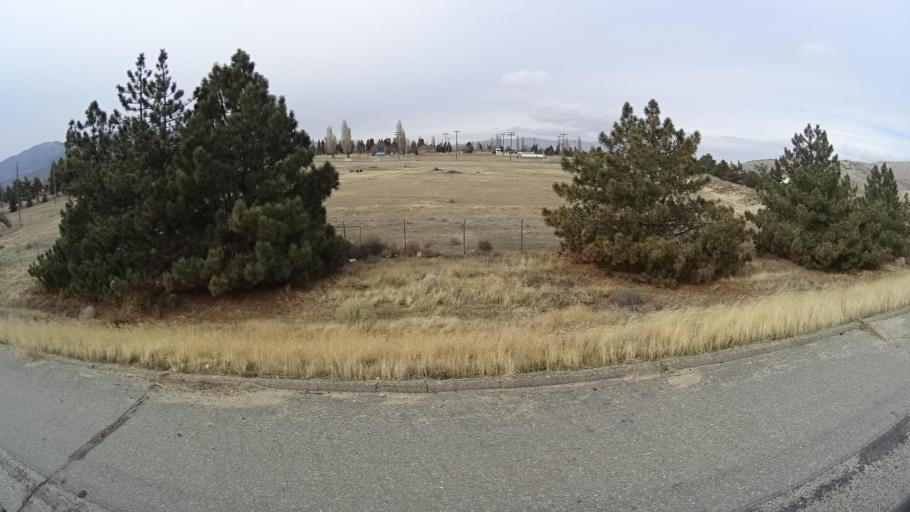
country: US
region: California
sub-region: Kern County
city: Tehachapi
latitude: 35.1196
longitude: -118.3966
